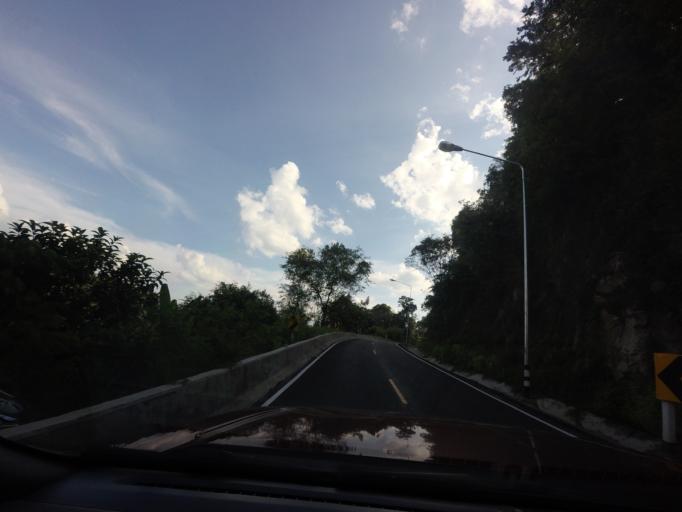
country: TH
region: Yala
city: Than To
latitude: 6.1348
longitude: 101.2985
